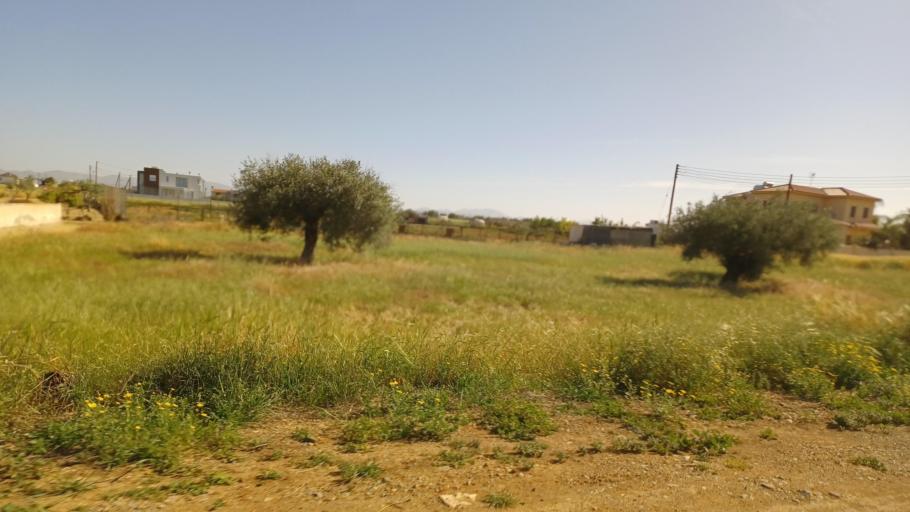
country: CY
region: Lefkosia
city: Kokkinotrimithia
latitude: 35.1519
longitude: 33.1912
